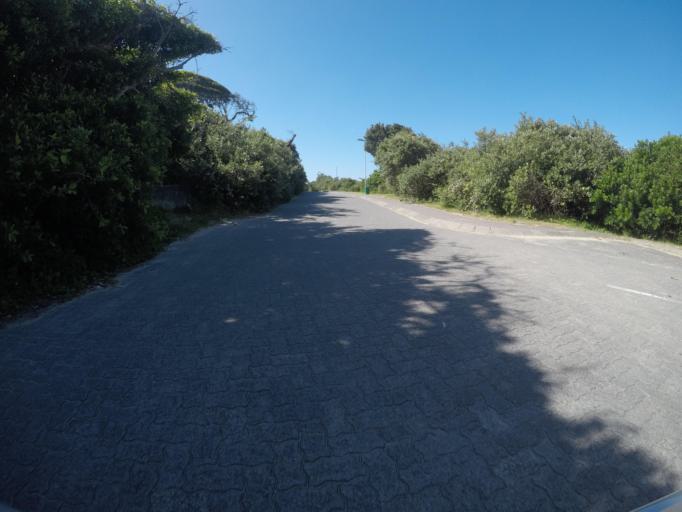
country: ZA
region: Eastern Cape
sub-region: Buffalo City Metropolitan Municipality
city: East London
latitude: -32.9874
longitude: 27.9490
